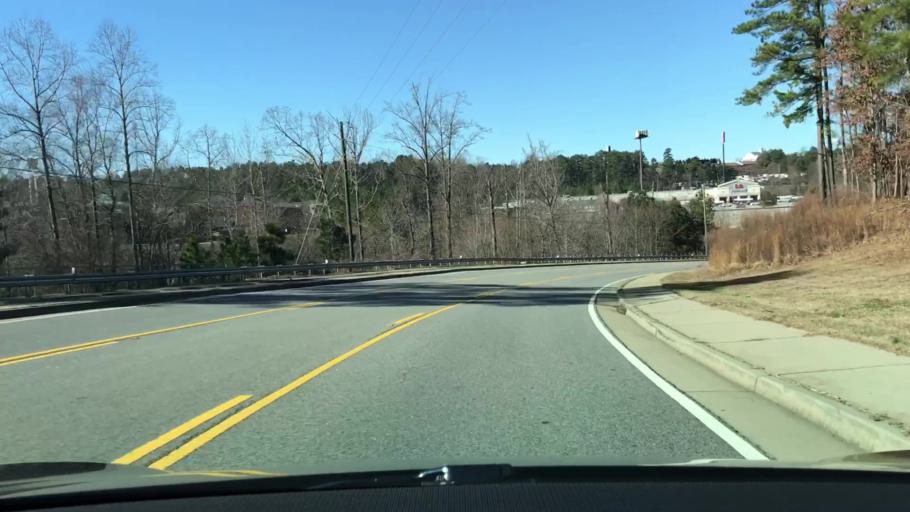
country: US
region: Georgia
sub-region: Forsyth County
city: Cumming
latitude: 34.1875
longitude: -84.1281
